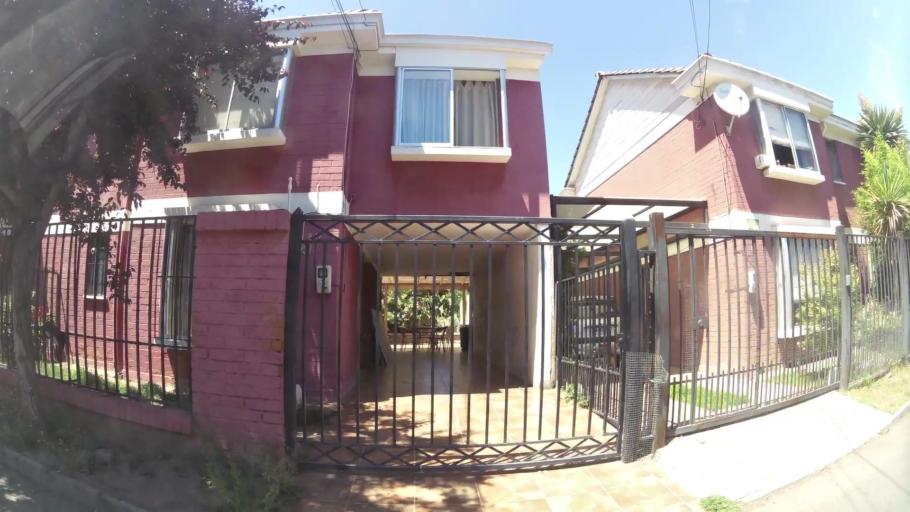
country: CL
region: Santiago Metropolitan
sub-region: Provincia de Maipo
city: San Bernardo
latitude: -33.6223
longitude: -70.7124
